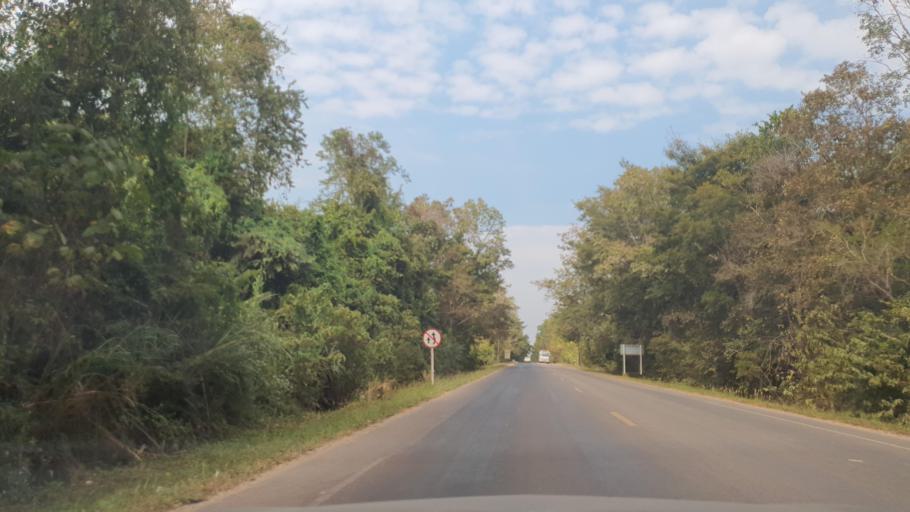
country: TH
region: Changwat Bueng Kan
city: Si Wilai
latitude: 18.2839
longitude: 103.8269
